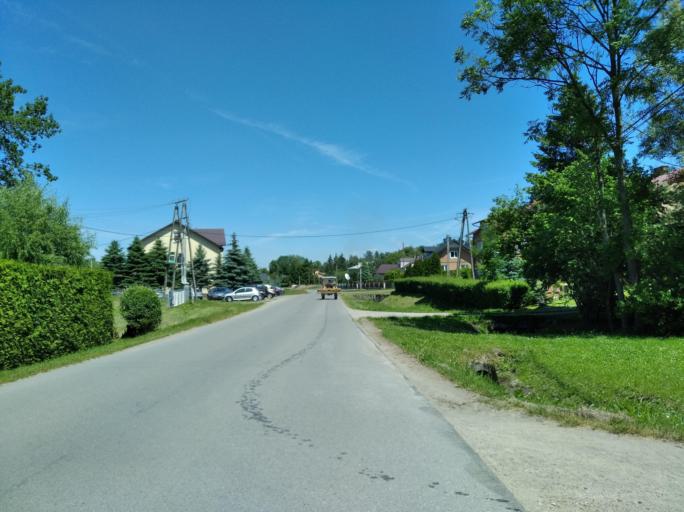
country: PL
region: Subcarpathian Voivodeship
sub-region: Powiat jasielski
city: Tarnowiec
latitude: 49.6943
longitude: 21.5534
